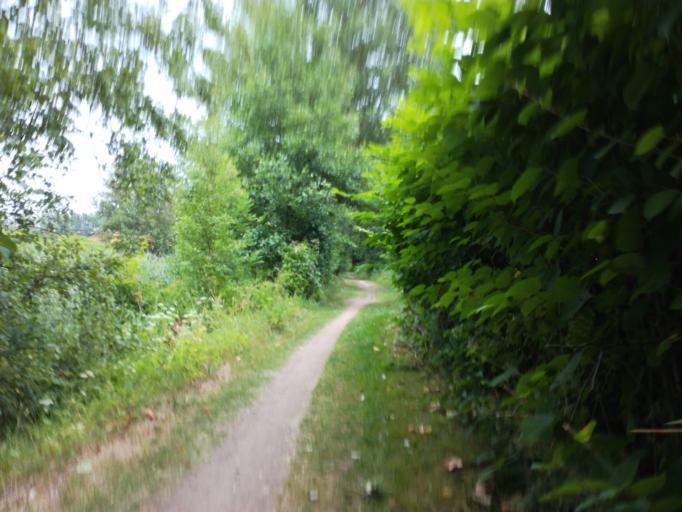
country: DK
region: South Denmark
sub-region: Vejle Kommune
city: Vejle
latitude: 55.7021
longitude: 9.5508
